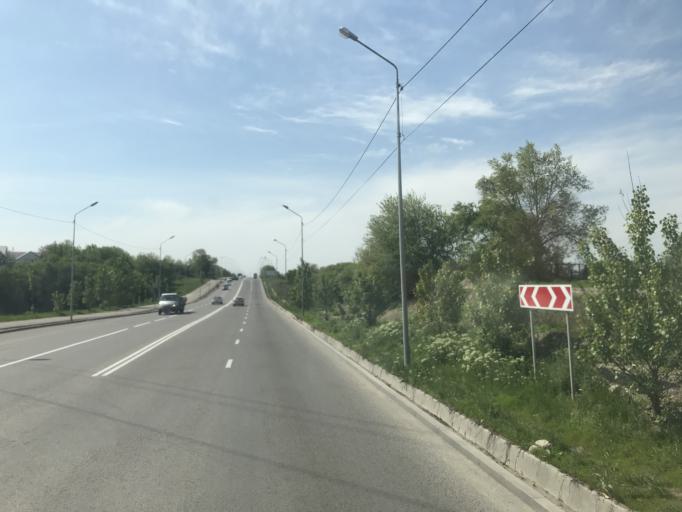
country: KZ
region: Almaty Qalasy
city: Almaty
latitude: 43.3037
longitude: 76.8885
